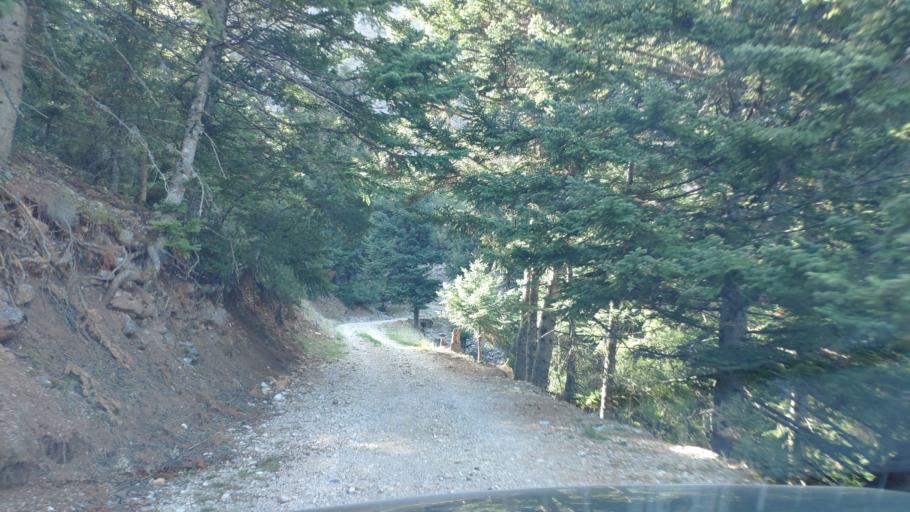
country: GR
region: West Greece
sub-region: Nomos Achaias
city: Aiyira
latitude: 37.9826
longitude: 22.3432
